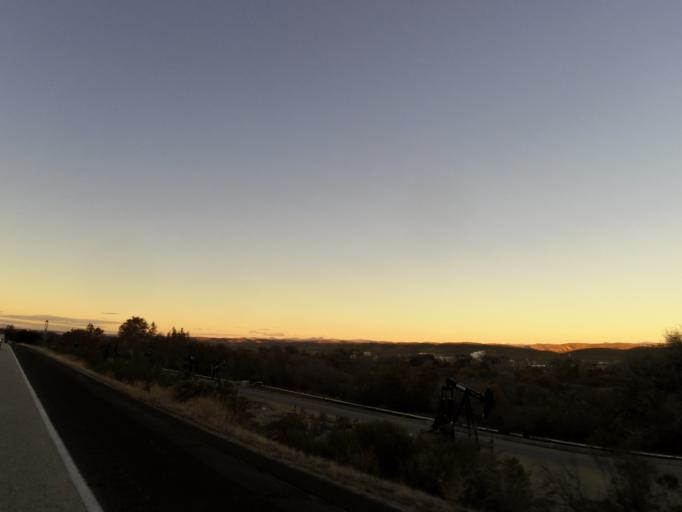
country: US
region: California
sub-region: San Luis Obispo County
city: Lake Nacimiento
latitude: 35.9516
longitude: -120.8787
